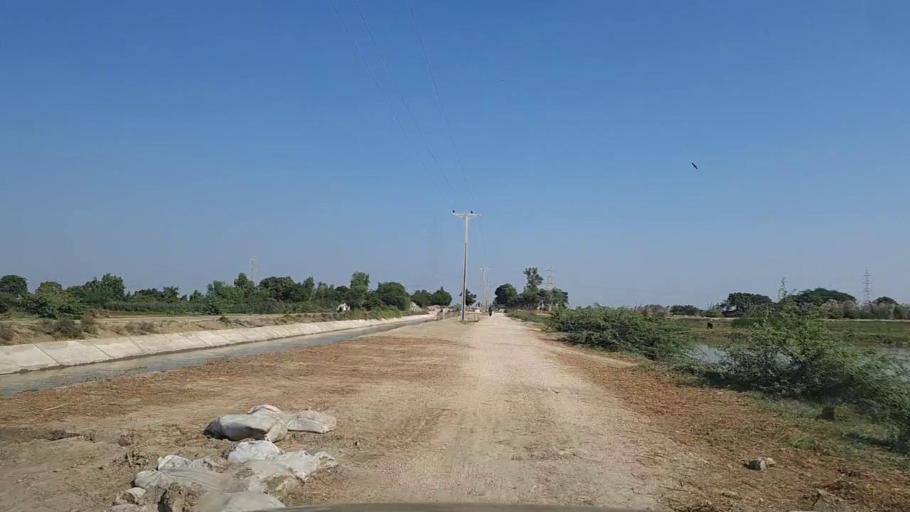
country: PK
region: Sindh
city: Thatta
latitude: 24.5961
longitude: 67.8173
